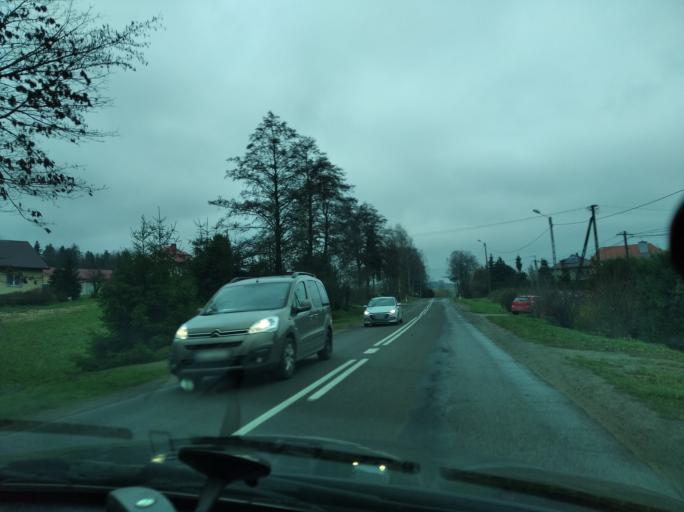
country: PL
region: Subcarpathian Voivodeship
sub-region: Powiat przeworski
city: Jawornik Polski
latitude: 49.8658
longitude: 22.2467
